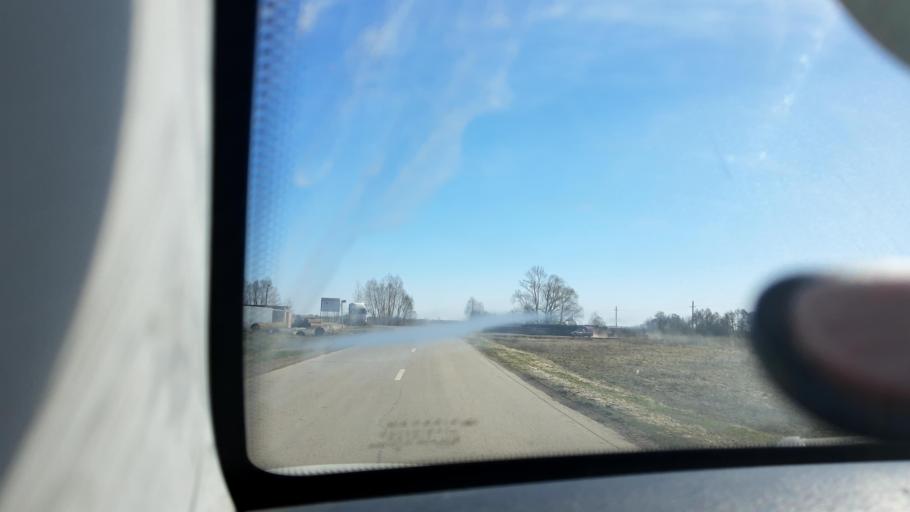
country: RU
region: Bashkortostan
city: Blagoveshchensk
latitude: 55.0060
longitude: 55.7354
